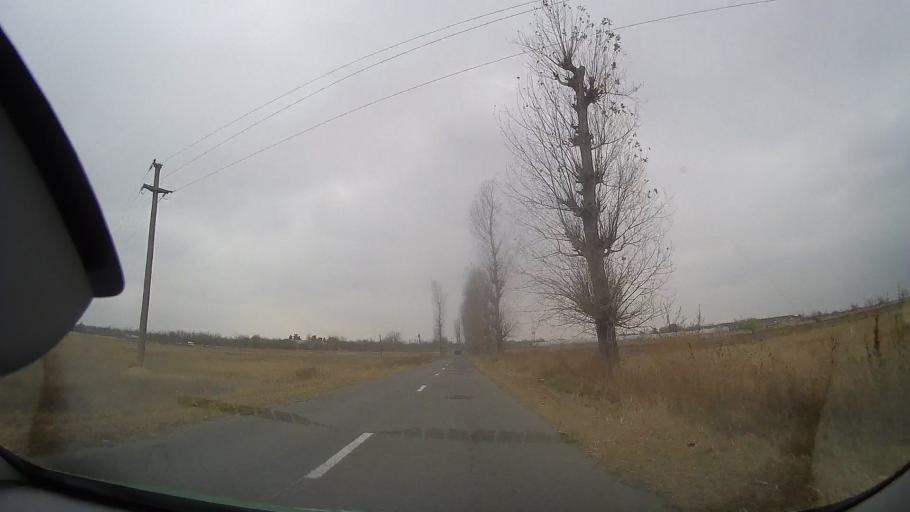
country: RO
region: Ialomita
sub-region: Comuna Valea Macrisului
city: Valea Macrisului
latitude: 44.7381
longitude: 26.8448
